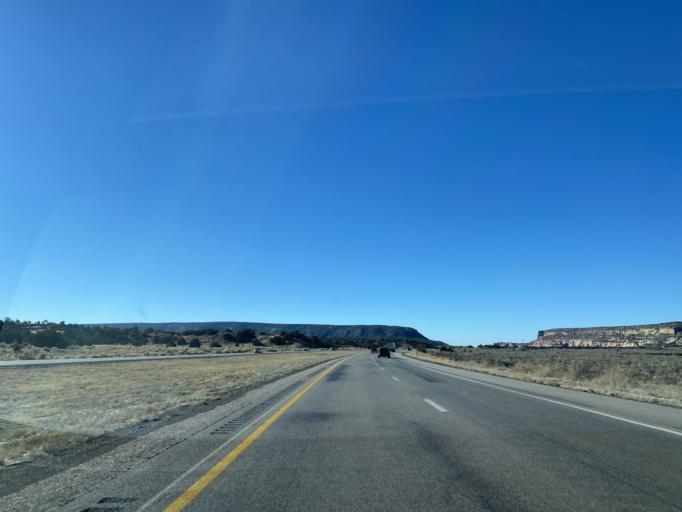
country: US
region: Arizona
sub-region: Apache County
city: Houck
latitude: 35.3872
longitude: -109.0121
